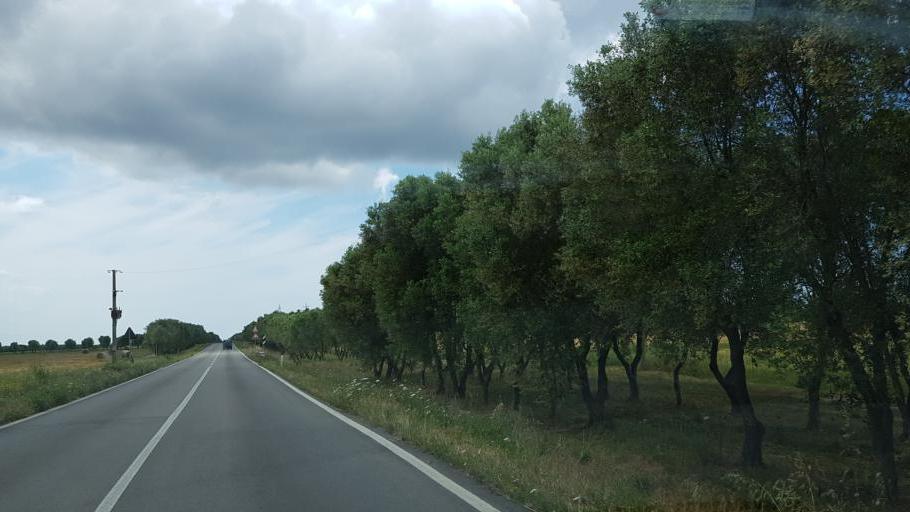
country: IT
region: Apulia
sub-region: Provincia di Brindisi
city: San Pancrazio Salentino
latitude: 40.3675
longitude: 17.8405
